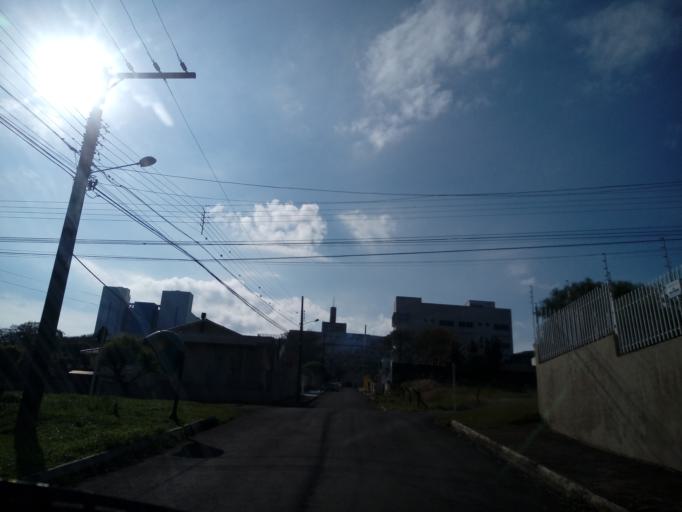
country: BR
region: Santa Catarina
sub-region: Chapeco
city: Chapeco
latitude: -27.1089
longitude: -52.6008
